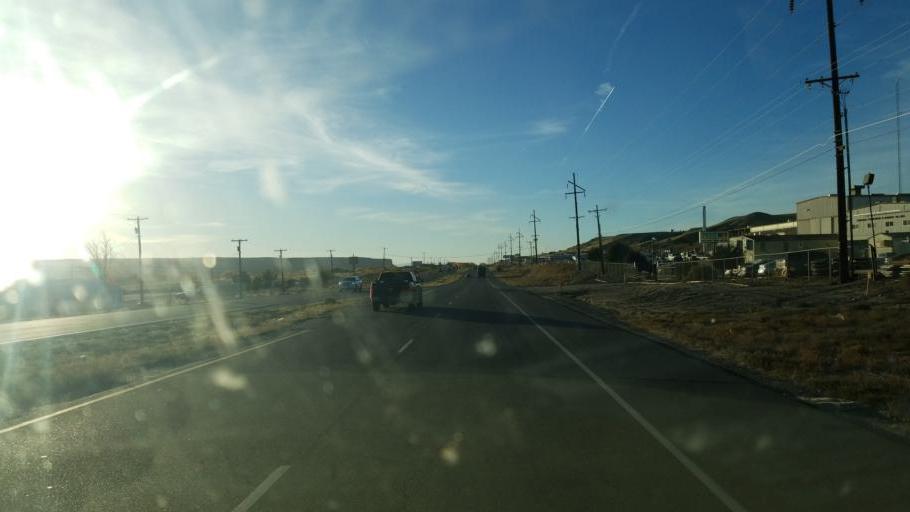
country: US
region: New Mexico
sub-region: San Juan County
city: Lee Acres
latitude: 36.7043
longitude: -108.1062
